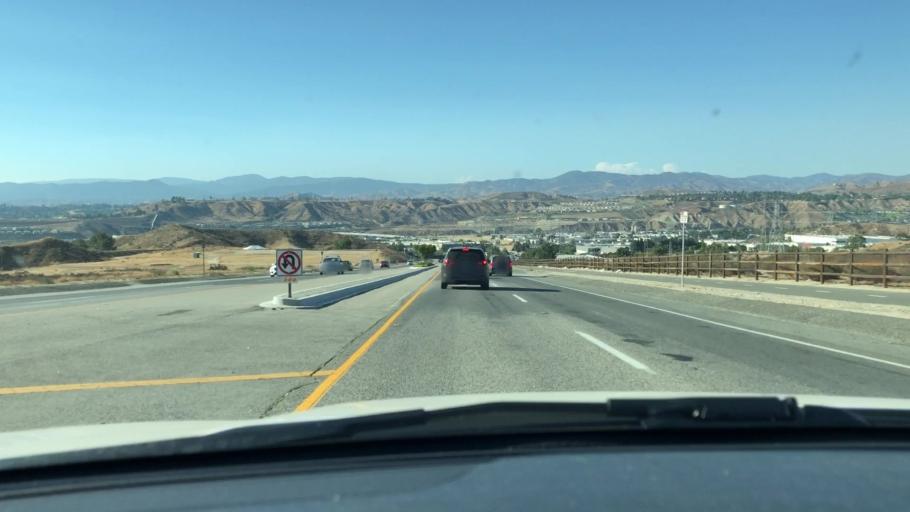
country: US
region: California
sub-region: Los Angeles County
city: Santa Clarita
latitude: 34.4042
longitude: -118.5032
